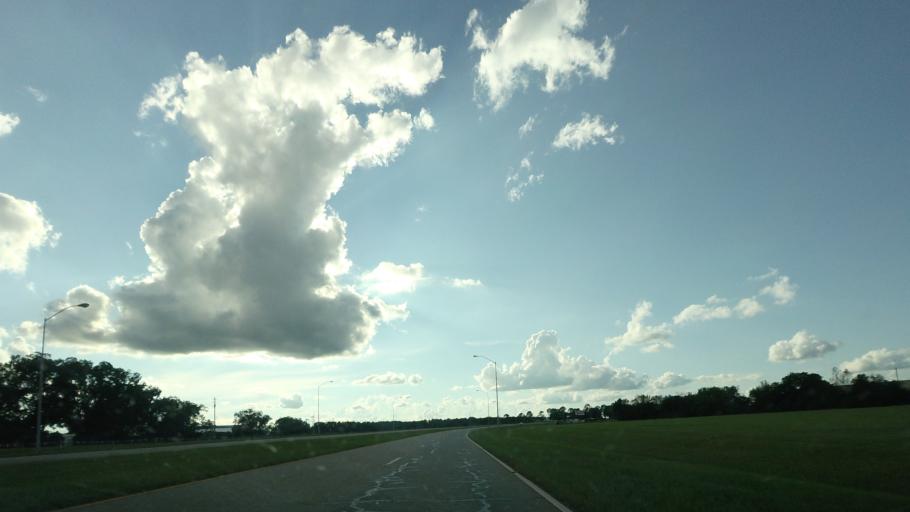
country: US
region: Georgia
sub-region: Houston County
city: Perry
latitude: 32.4421
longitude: -83.7441
